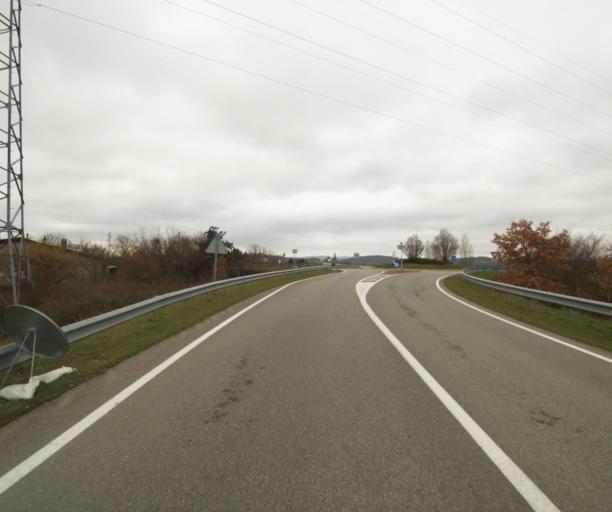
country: FR
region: Midi-Pyrenees
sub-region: Departement de l'Ariege
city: Pamiers
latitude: 43.1375
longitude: 1.6272
